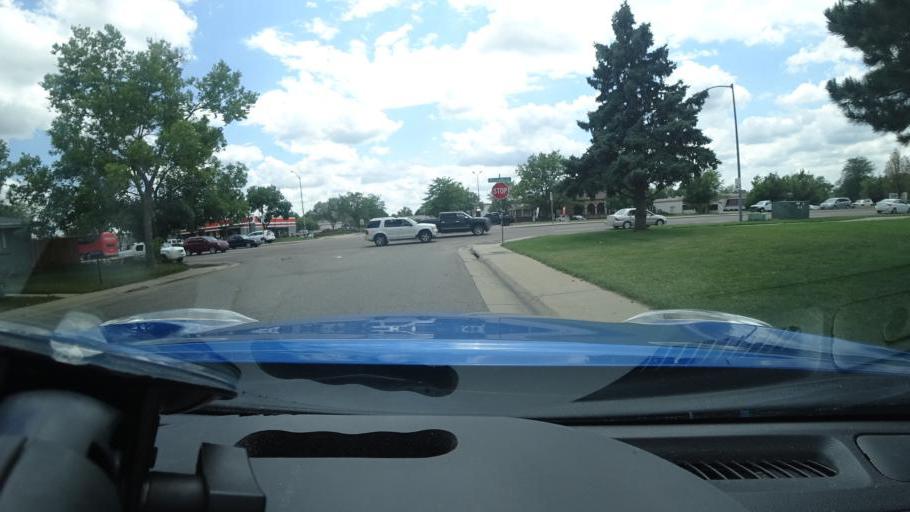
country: US
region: Colorado
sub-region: Adams County
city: Aurora
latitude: 39.6970
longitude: -104.8352
